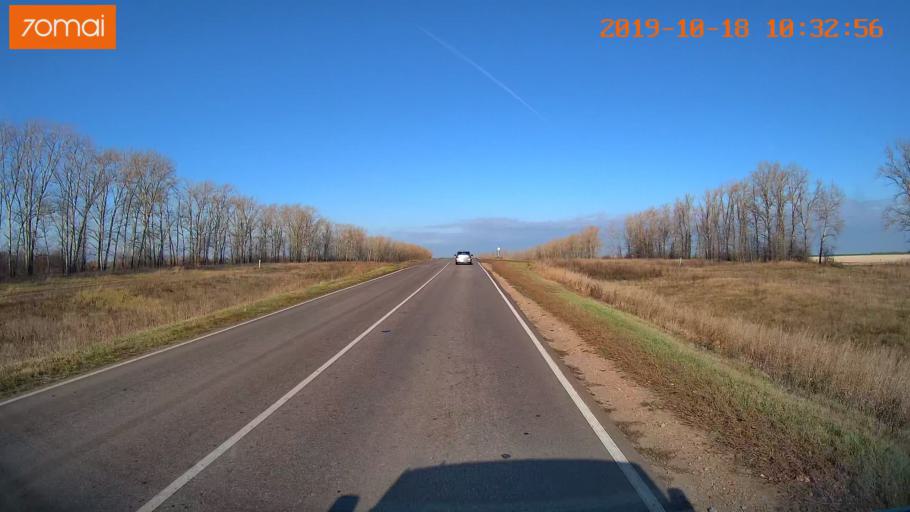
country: RU
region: Tula
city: Kurkino
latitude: 53.5014
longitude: 38.6194
